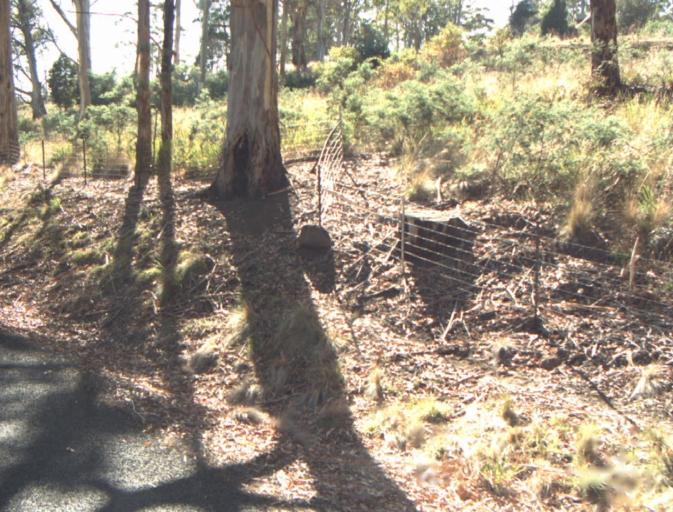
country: AU
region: Tasmania
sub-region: Launceston
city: Newstead
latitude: -41.3679
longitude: 147.3017
